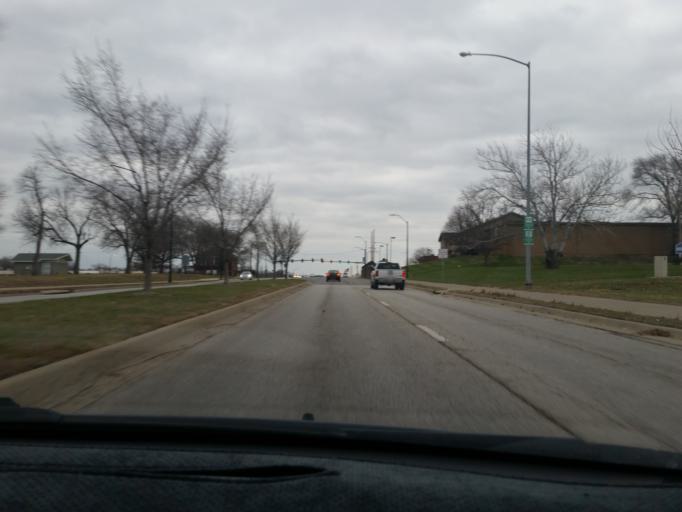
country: US
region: Kansas
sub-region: Douglas County
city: Lawrence
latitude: 38.9427
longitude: -95.2639
